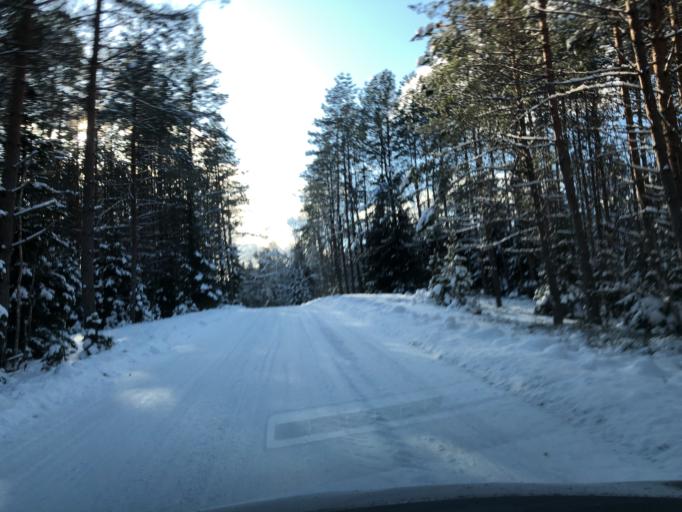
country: EE
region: Jaervamaa
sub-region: Paide linn
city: Paide
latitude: 59.0600
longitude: 25.5112
